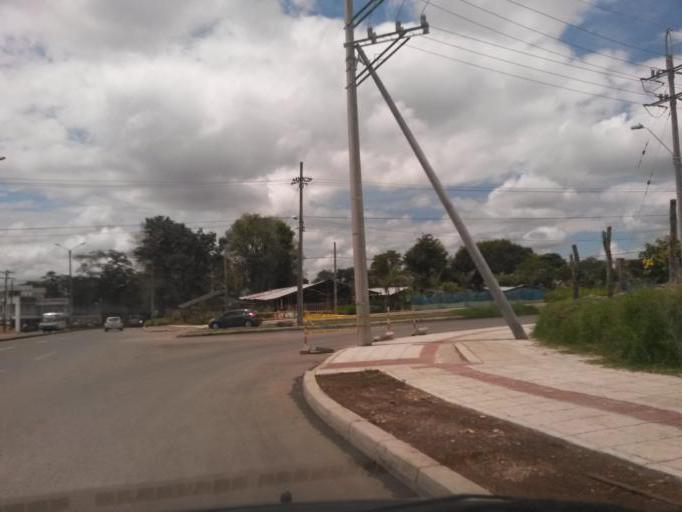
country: CO
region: Cauca
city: Popayan
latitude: 2.4776
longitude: -76.5769
